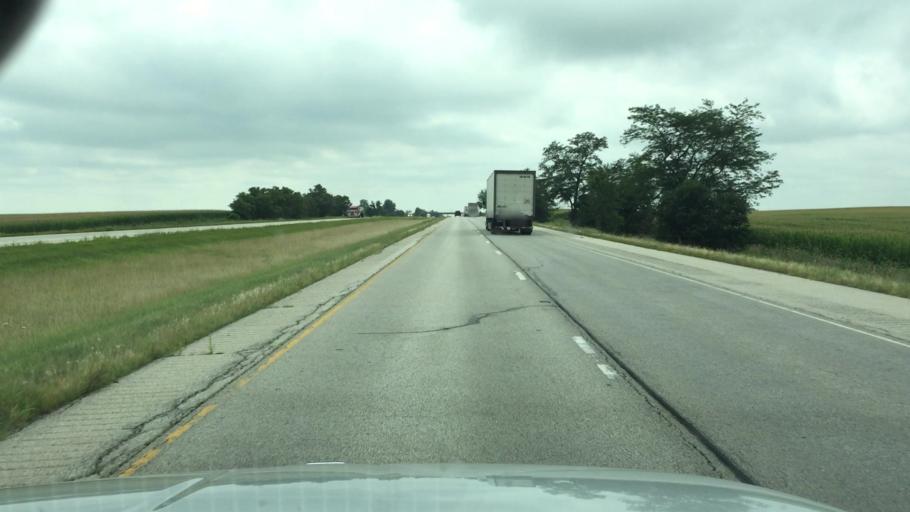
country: US
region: Illinois
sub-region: Knox County
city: Galesburg
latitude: 41.0328
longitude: -90.3347
